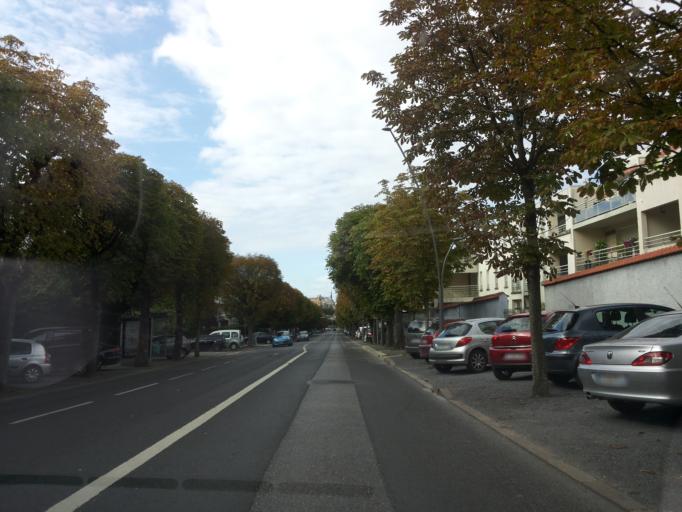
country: FR
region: Champagne-Ardenne
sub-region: Departement de la Marne
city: Reims
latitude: 49.2443
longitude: 4.0495
